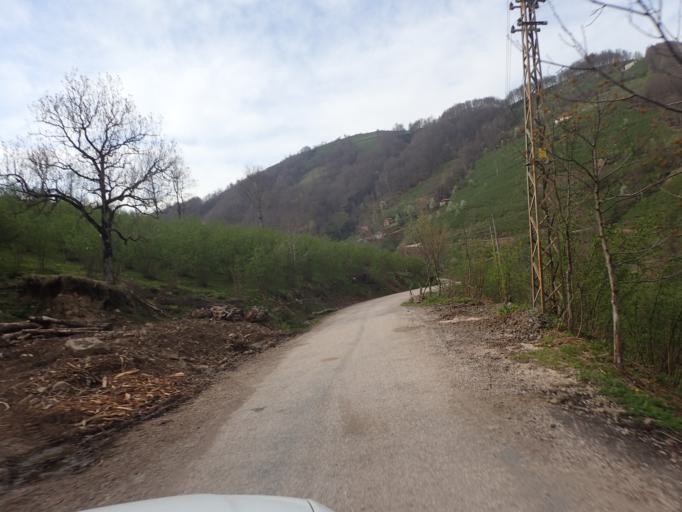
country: TR
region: Ordu
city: Aybasti
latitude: 40.6993
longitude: 37.2800
